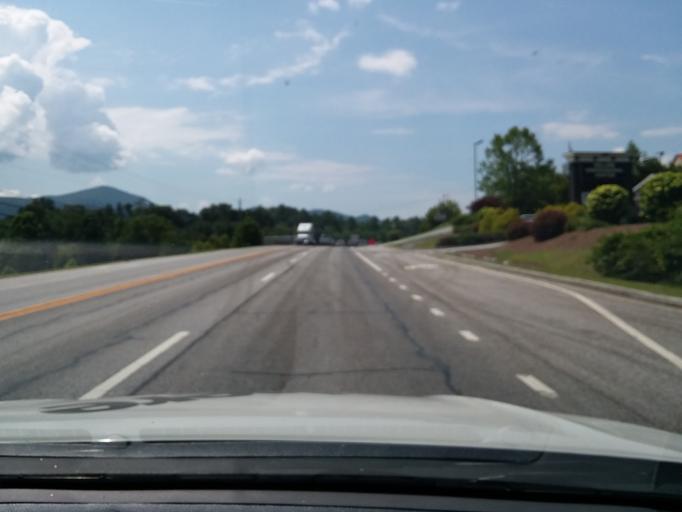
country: US
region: Georgia
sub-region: Rabun County
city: Mountain City
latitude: 34.9783
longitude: -83.3837
